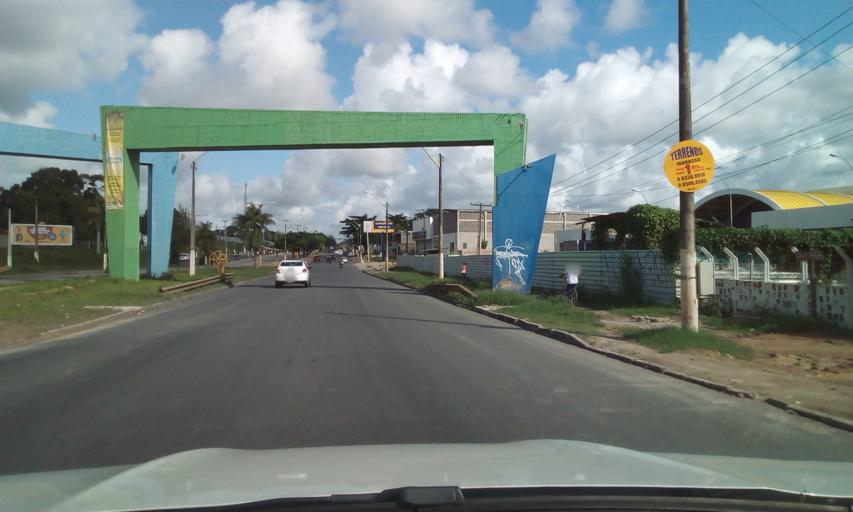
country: BR
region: Pernambuco
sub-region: Abreu E Lima
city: Abreu e Lima
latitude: -7.8862
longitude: -34.9045
